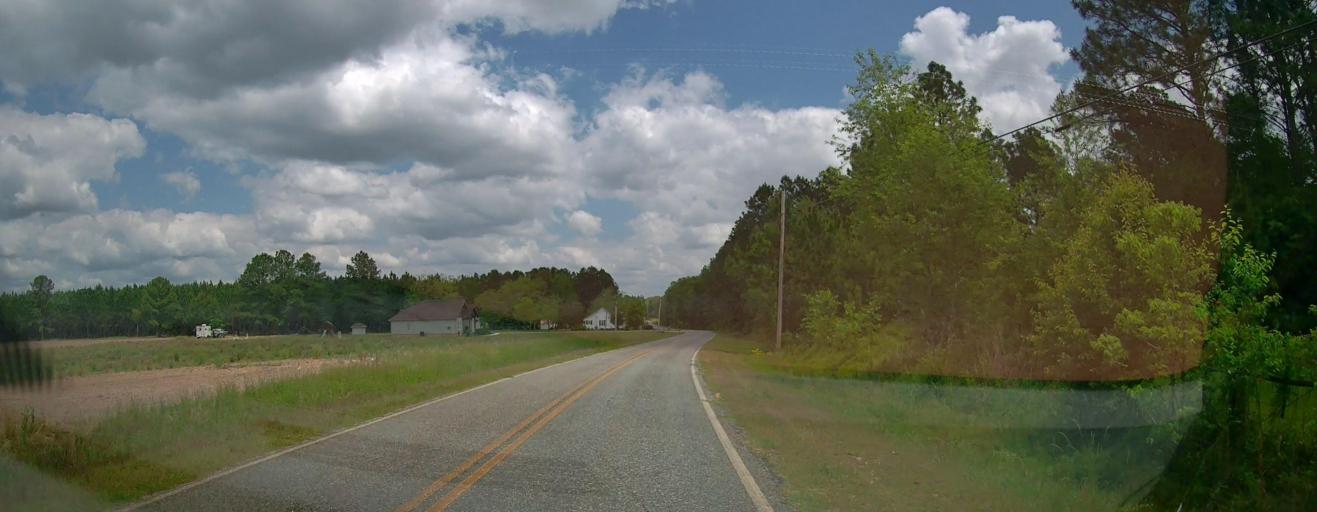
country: US
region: Georgia
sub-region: Laurens County
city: Dublin
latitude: 32.6020
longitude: -82.9507
